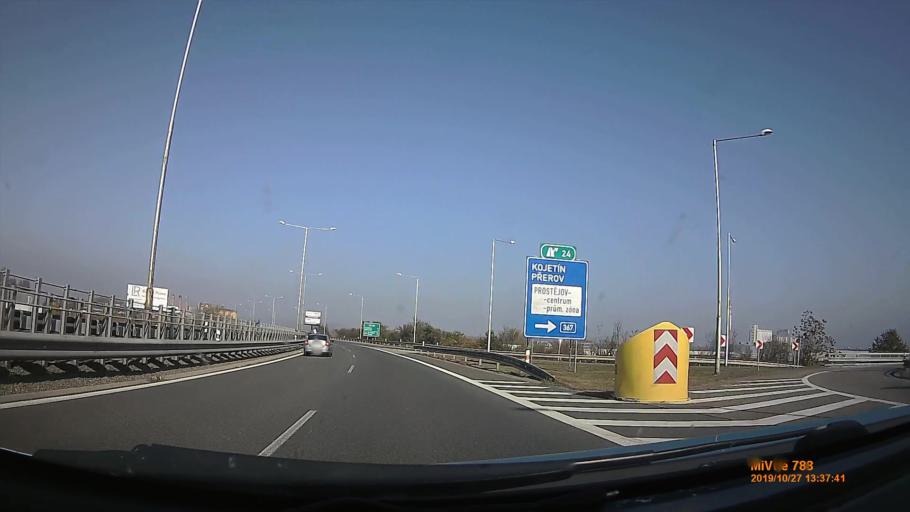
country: CZ
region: Olomoucky
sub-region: Okres Prostejov
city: Prostejov
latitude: 49.4686
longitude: 17.1329
